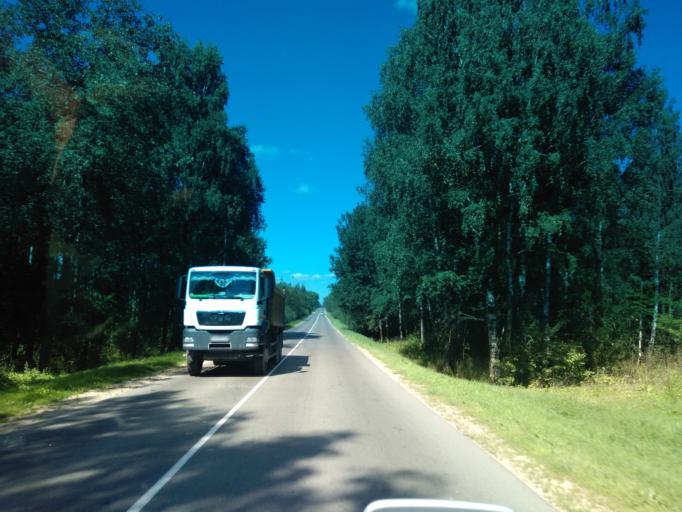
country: BY
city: Fanipol
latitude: 53.7055
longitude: 27.3503
